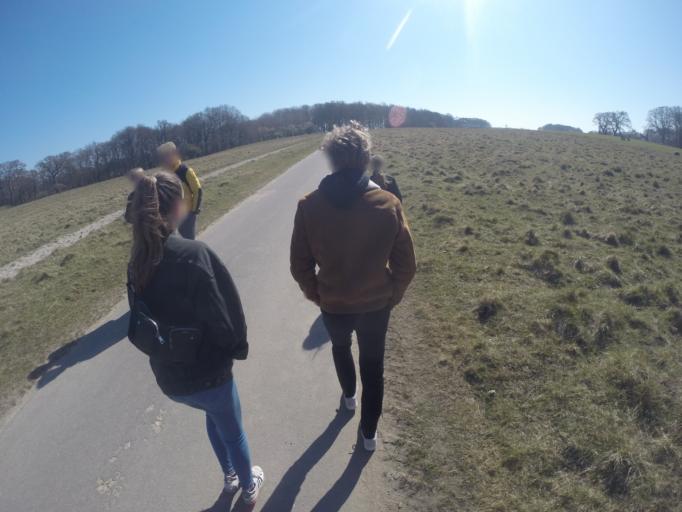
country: DK
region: Capital Region
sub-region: Rudersdal Kommune
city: Trorod
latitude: 55.8001
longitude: 12.5719
